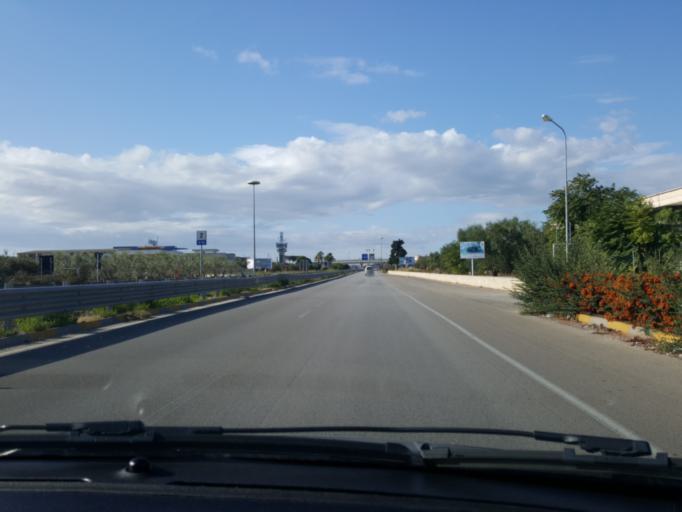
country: IT
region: Apulia
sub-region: Provincia di Bari
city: Triggiano
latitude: 41.0875
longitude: 16.9481
